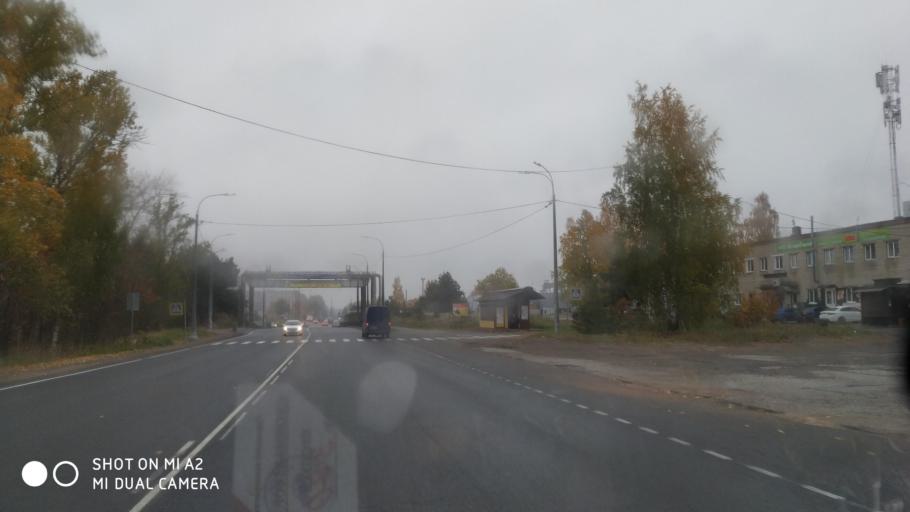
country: RU
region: Leningrad
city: Sosnovyy Bor
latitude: 59.8809
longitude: 29.0948
